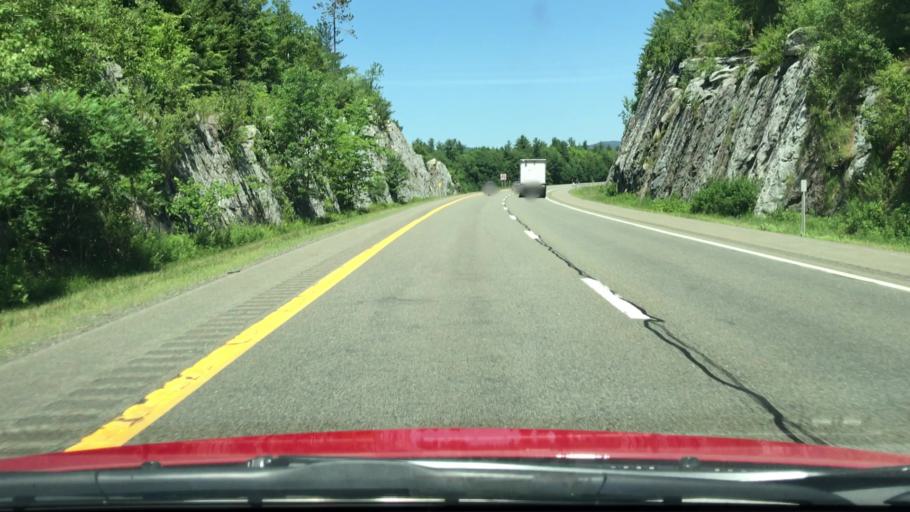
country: US
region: New York
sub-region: Essex County
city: Elizabethtown
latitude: 44.3332
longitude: -73.5327
